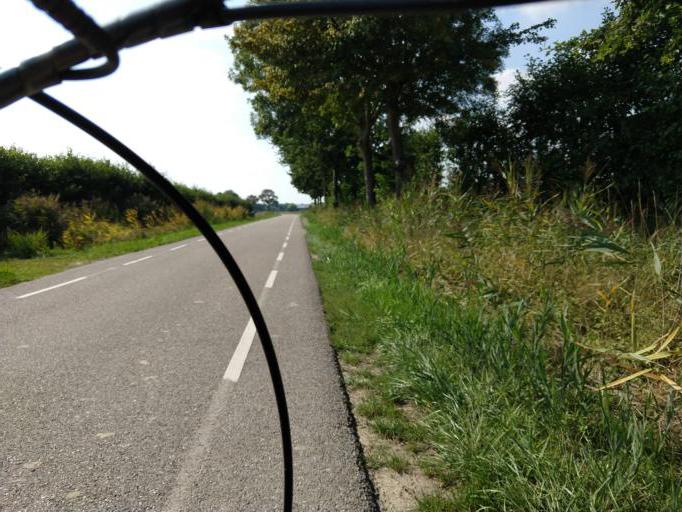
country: NL
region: Zeeland
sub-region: Gemeente Terneuzen
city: Terneuzen
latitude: 51.4092
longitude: 3.8707
